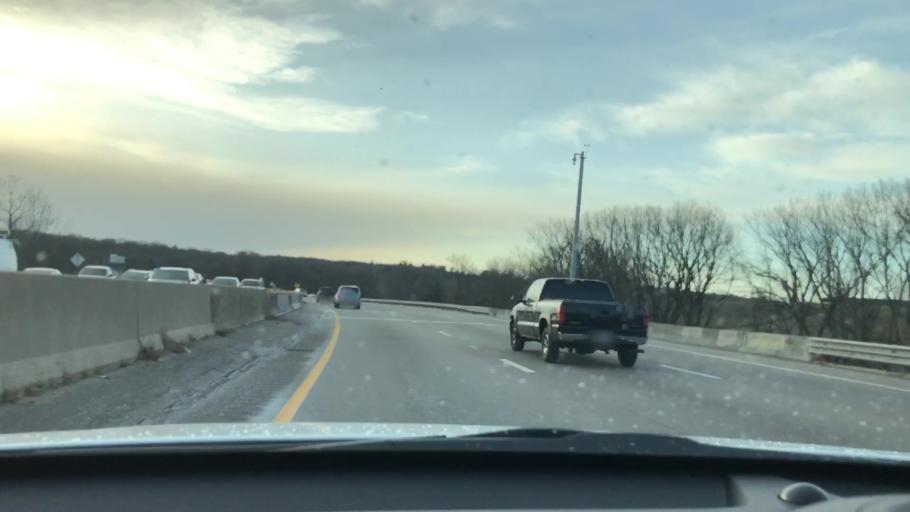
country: US
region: Massachusetts
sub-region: Norfolk County
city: Braintree
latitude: 42.2095
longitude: -70.9962
